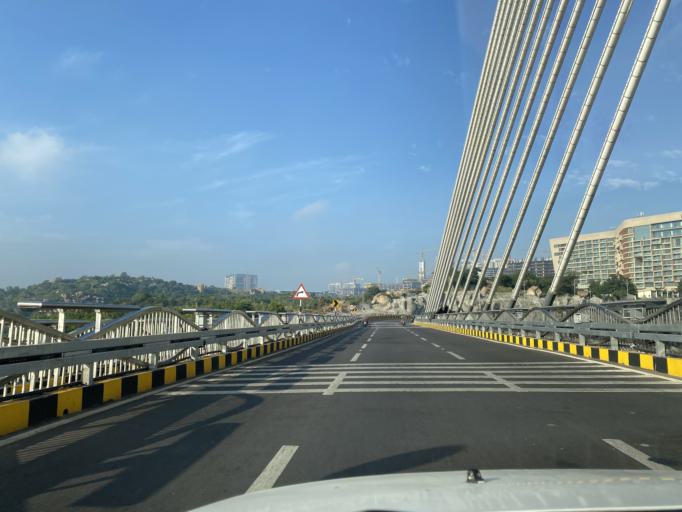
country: IN
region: Telangana
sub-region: Rangareddi
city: Kukatpalli
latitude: 17.4315
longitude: 78.3891
